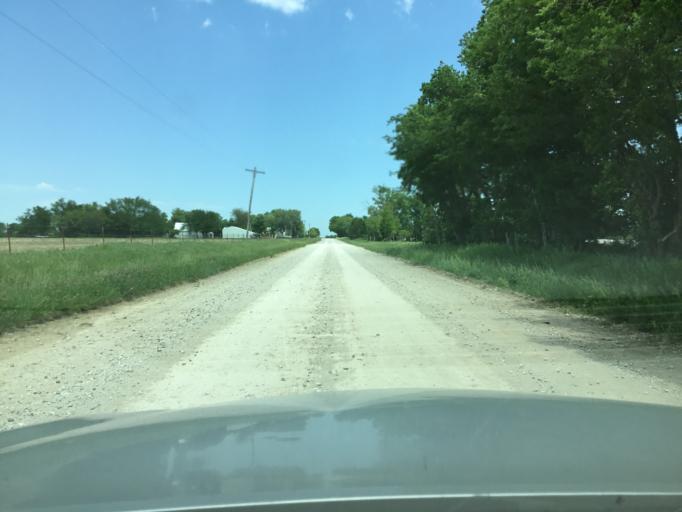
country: US
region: Kansas
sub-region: Montgomery County
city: Independence
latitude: 37.0990
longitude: -95.7829
